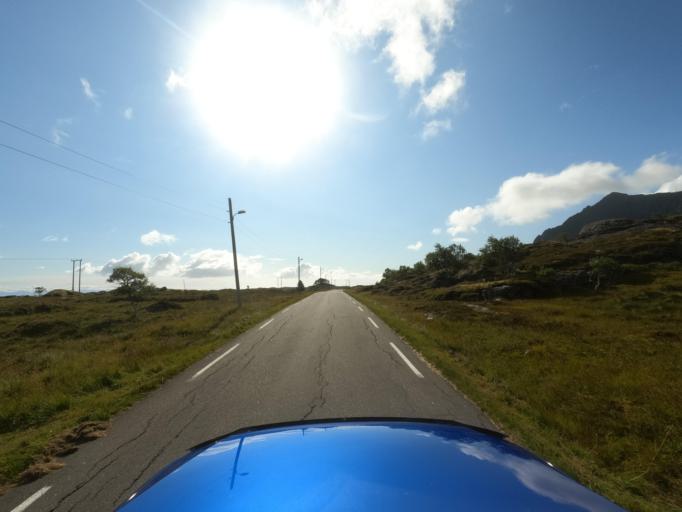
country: NO
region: Nordland
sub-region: Vestvagoy
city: Evjen
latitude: 68.2111
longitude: 14.0547
